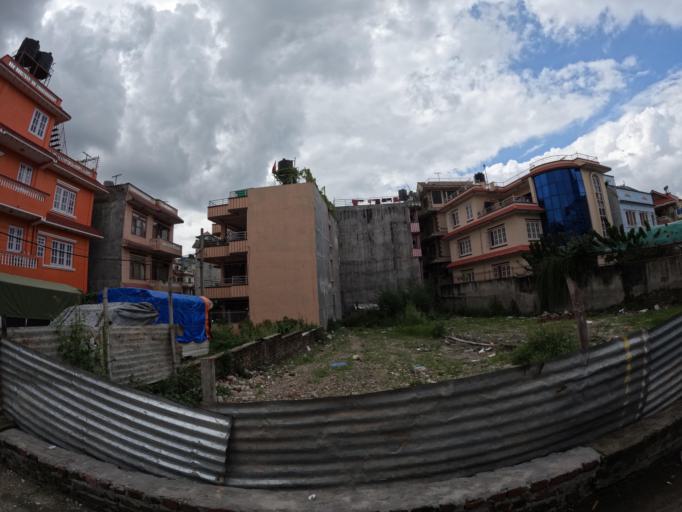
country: NP
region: Central Region
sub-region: Bagmati Zone
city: Kathmandu
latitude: 27.7400
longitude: 85.3154
